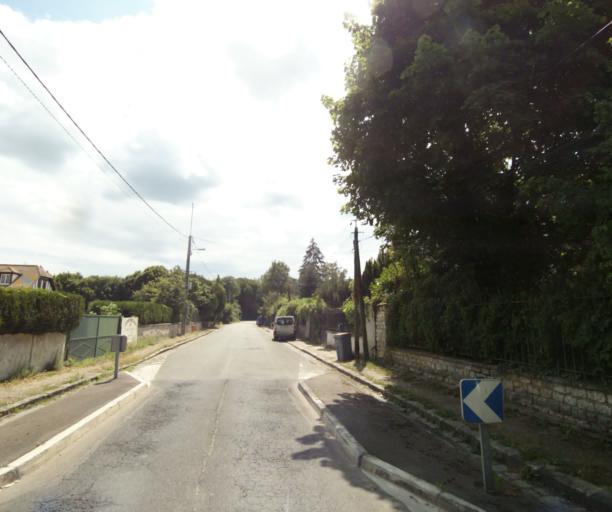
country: FR
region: Ile-de-France
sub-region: Departement de Seine-et-Marne
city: Bois-le-Roi
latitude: 48.4664
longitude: 2.7108
